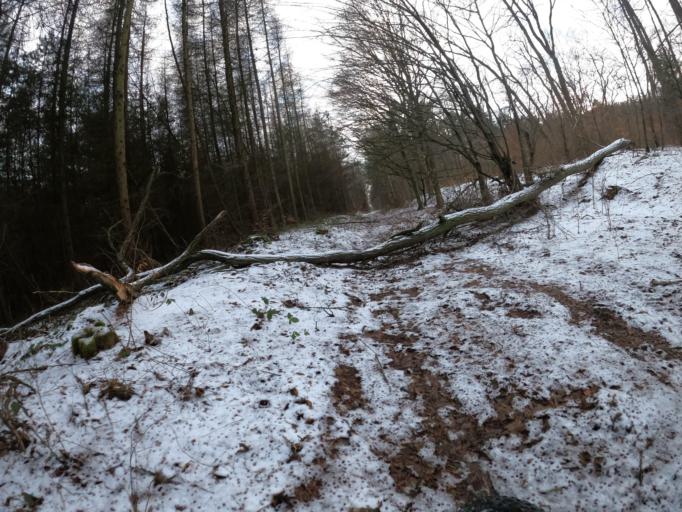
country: PL
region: Lubusz
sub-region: Powiat slubicki
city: Cybinka
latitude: 52.1900
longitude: 14.8737
